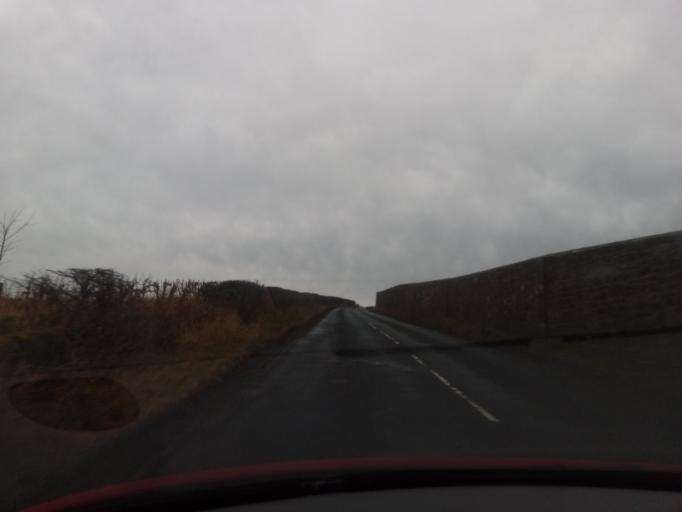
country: GB
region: England
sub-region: Northumberland
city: Alnwick
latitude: 55.4439
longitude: -1.7361
